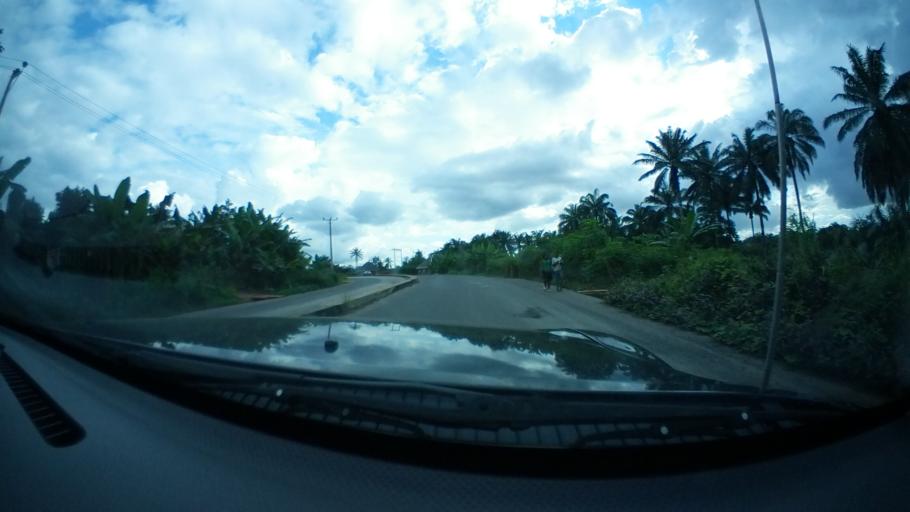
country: NG
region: Imo
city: Orlu
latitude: 5.8176
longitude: 7.0684
